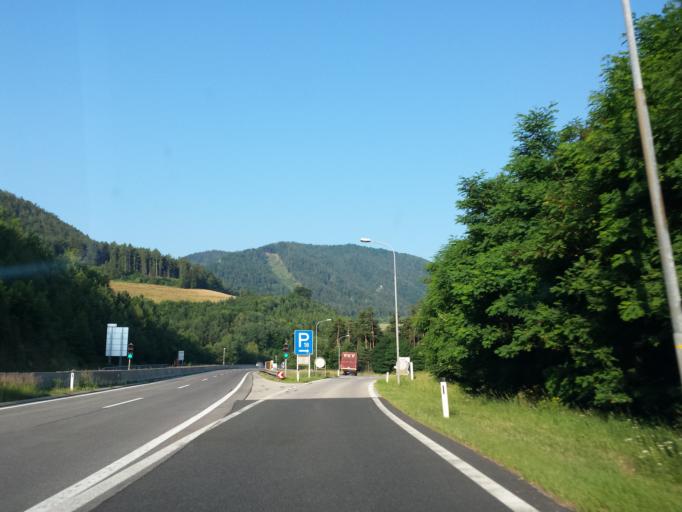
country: AT
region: Lower Austria
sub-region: Politischer Bezirk Neunkirchen
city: Gloggnitz
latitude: 47.6585
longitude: 15.9234
